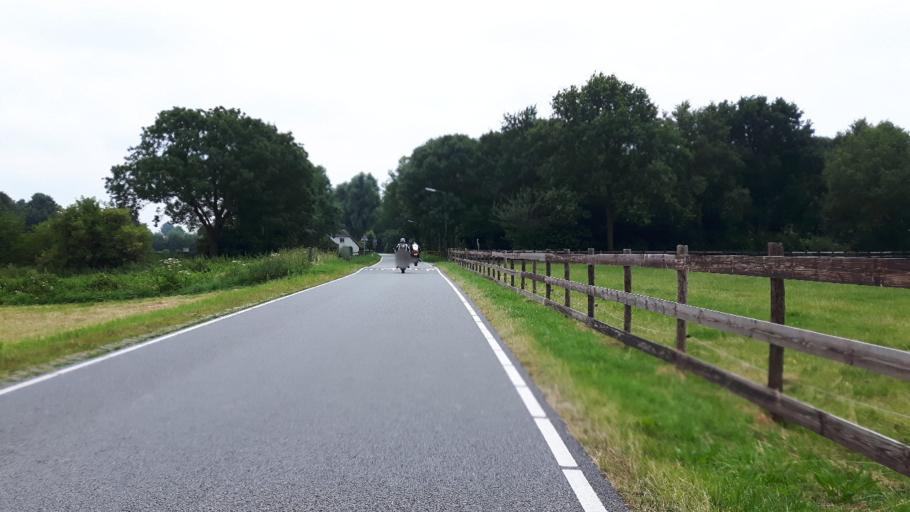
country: NL
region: Utrecht
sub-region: Gemeente IJsselstein
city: IJsselstein
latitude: 52.0373
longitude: 5.0370
